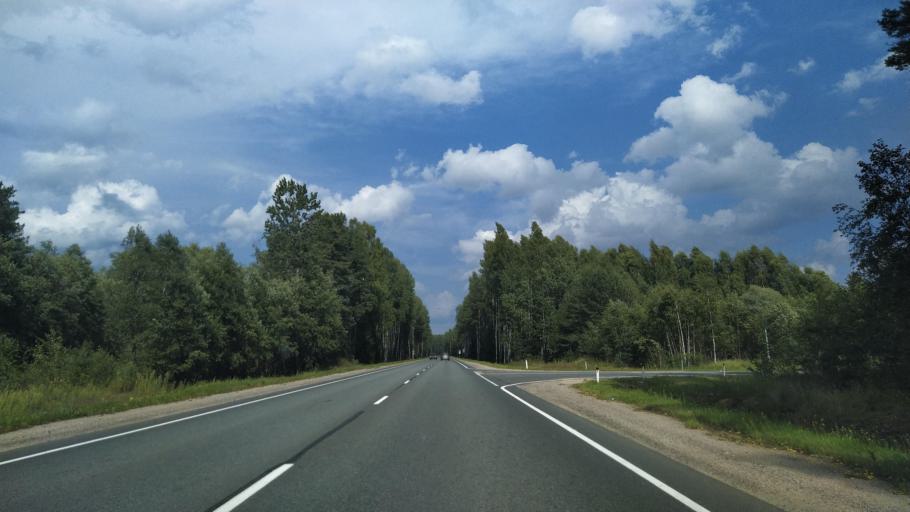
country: RU
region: Pskov
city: Porkhov
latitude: 57.8694
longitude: 29.6108
